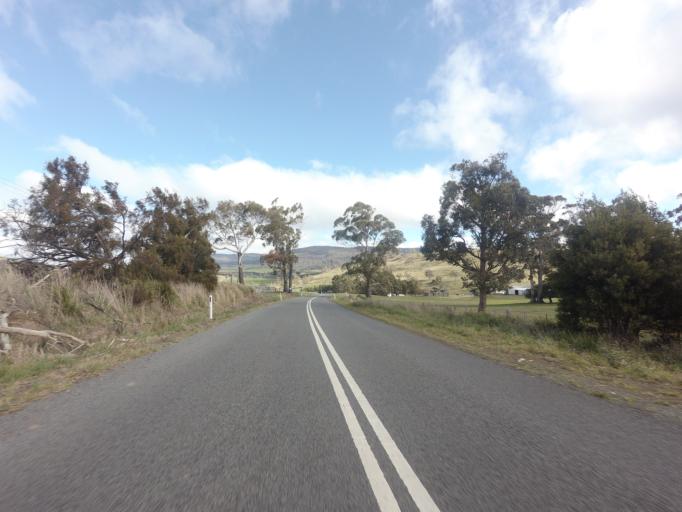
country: AU
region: Tasmania
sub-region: Derwent Valley
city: New Norfolk
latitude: -42.5582
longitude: 146.7077
